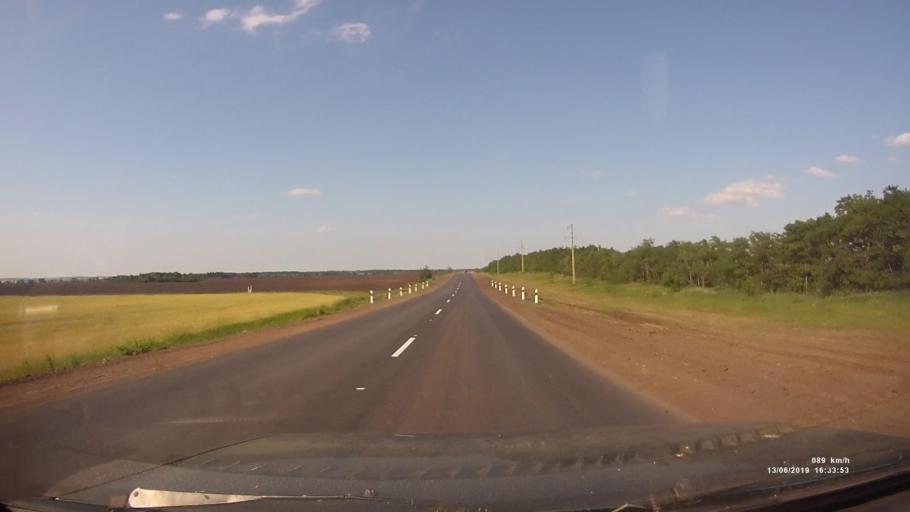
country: RU
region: Rostov
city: Kazanskaya
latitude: 49.8655
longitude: 41.2853
